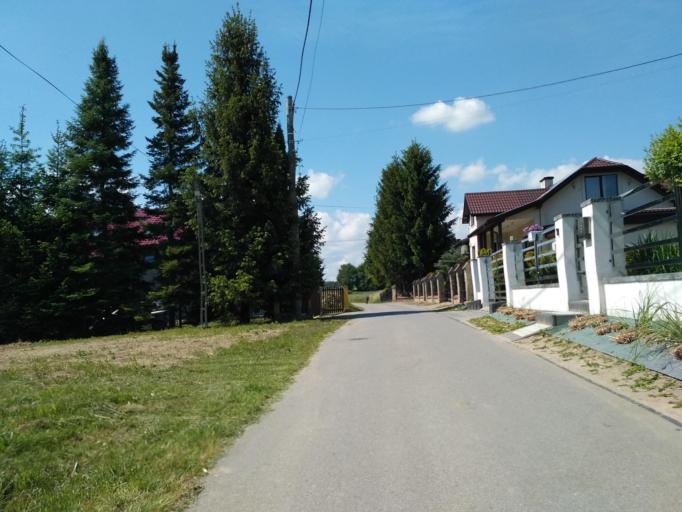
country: PL
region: Subcarpathian Voivodeship
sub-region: Powiat krosnienski
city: Miejsce Piastowe
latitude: 49.6481
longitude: 21.7588
